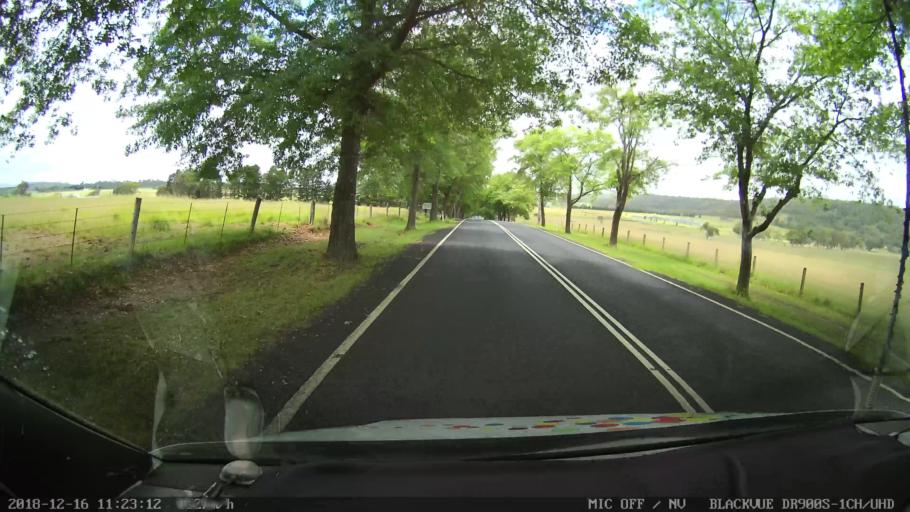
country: AU
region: New South Wales
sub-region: Tenterfield Municipality
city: Carrolls Creek
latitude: -29.0538
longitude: 152.0334
